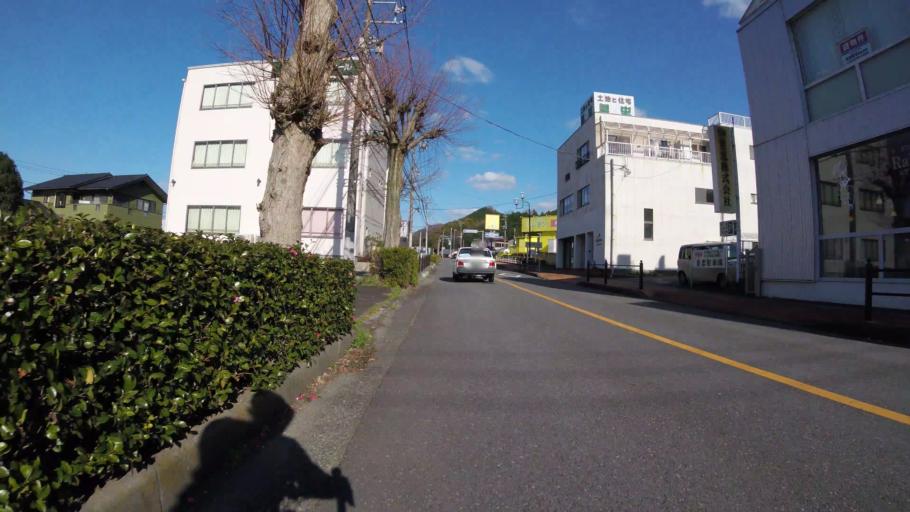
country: JP
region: Shizuoka
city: Ito
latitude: 34.9818
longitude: 138.9524
